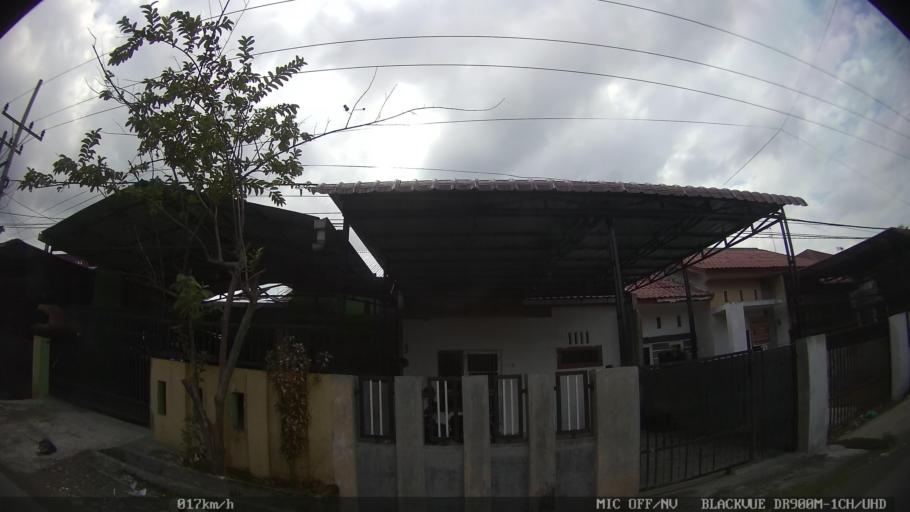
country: ID
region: North Sumatra
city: Sunggal
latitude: 3.6117
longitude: 98.6238
